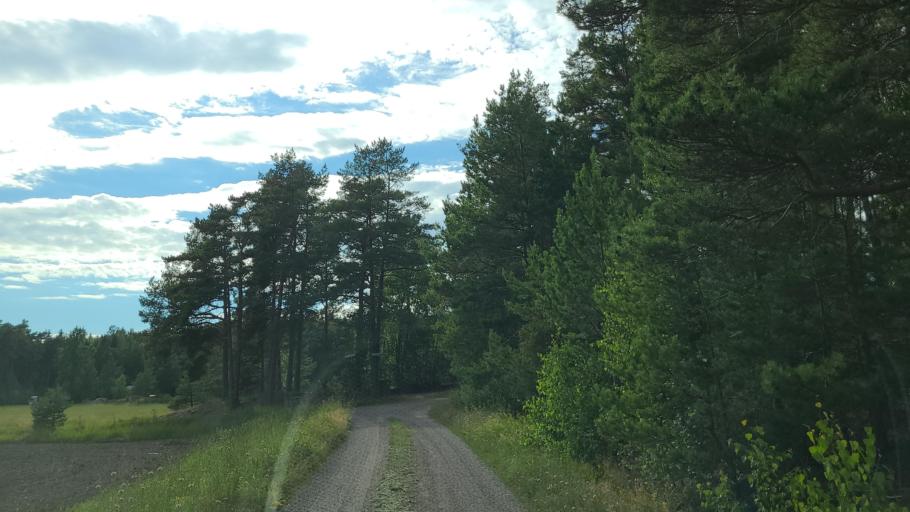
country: FI
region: Varsinais-Suomi
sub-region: Aboland-Turunmaa
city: Nagu
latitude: 60.2864
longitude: 21.9095
